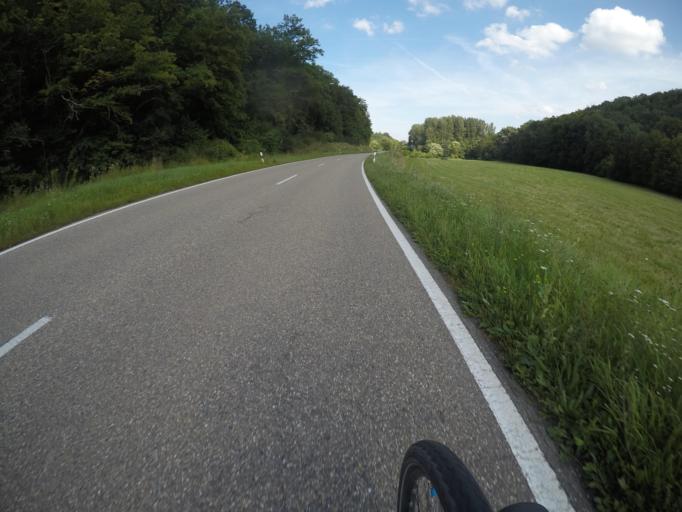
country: DE
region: Baden-Wuerttemberg
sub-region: Karlsruhe Region
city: Niefern-Oschelbronn
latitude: 48.9380
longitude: 8.7773
